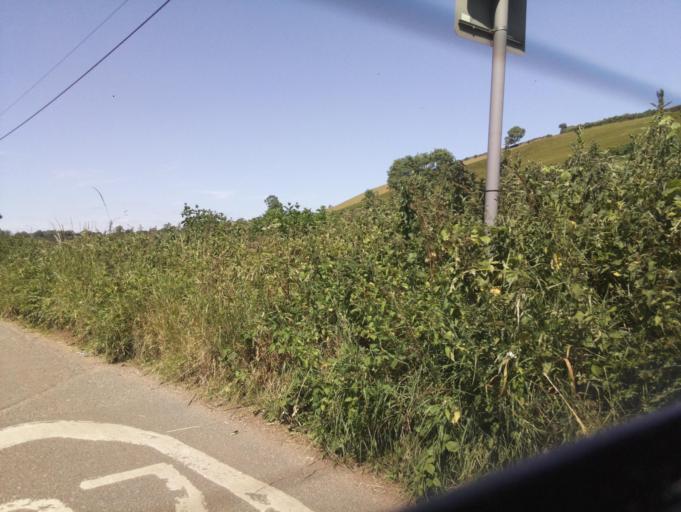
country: GB
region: England
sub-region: Devon
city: Marldon
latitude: 50.4748
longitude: -3.6015
